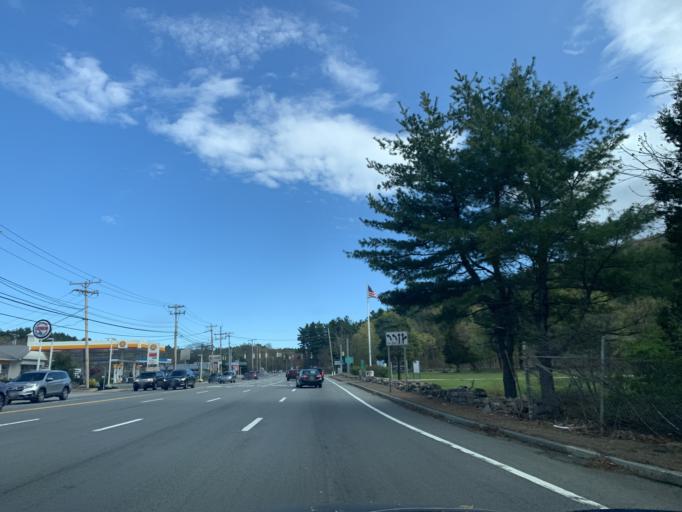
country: US
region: Massachusetts
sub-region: Norfolk County
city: Canton
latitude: 42.2069
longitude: -71.1195
